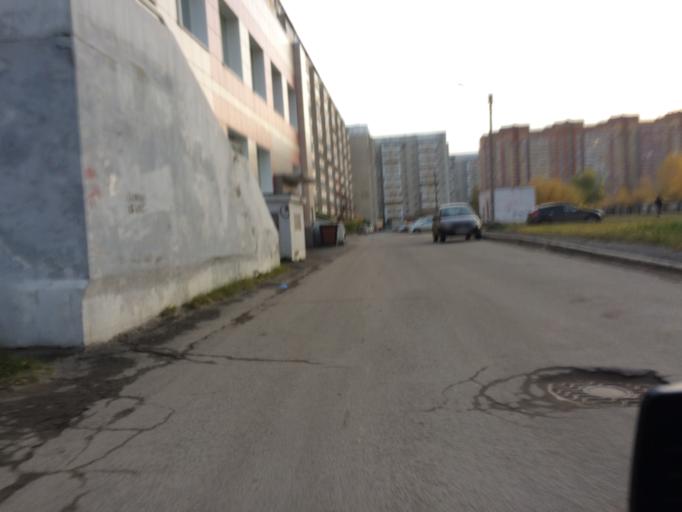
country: RU
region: Mariy-El
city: Yoshkar-Ola
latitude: 56.6335
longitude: 47.9297
